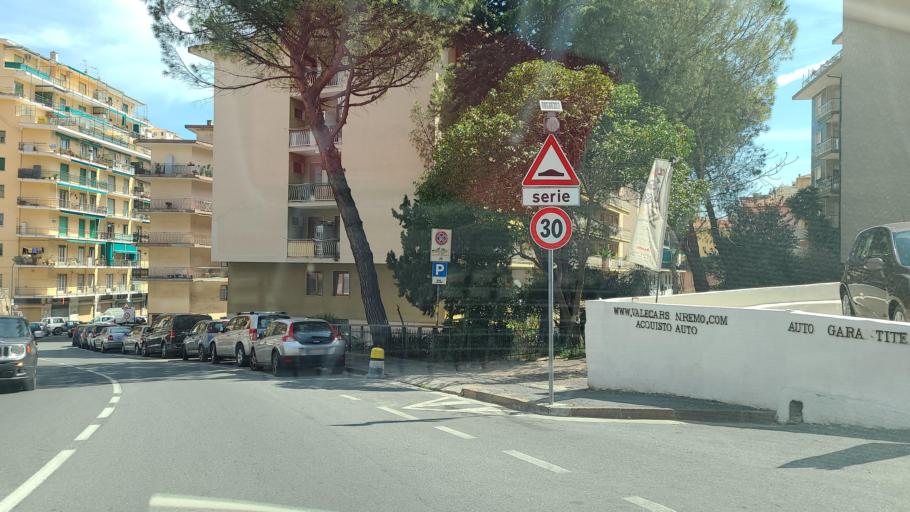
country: IT
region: Liguria
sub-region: Provincia di Imperia
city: San Remo
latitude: 43.8210
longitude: 7.7686
